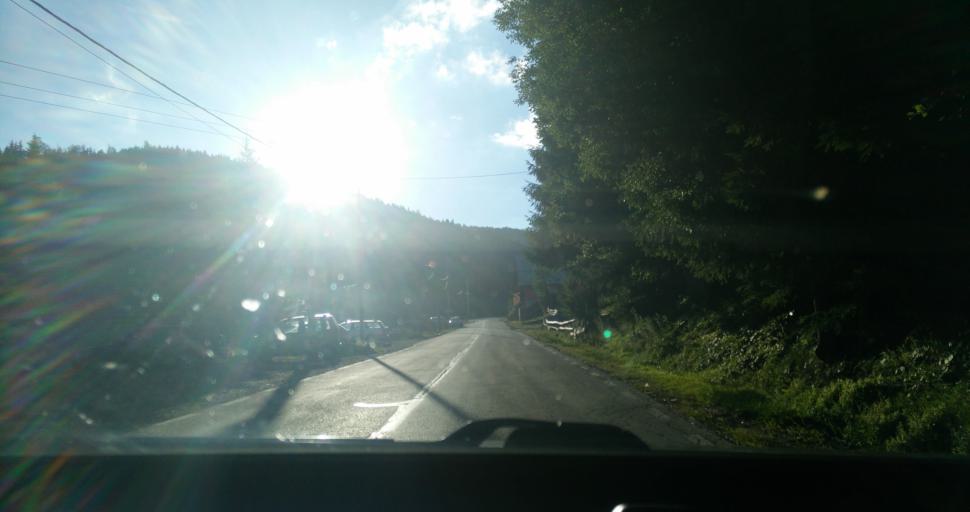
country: RO
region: Alba
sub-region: Comuna Arieseni
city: Arieseni
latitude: 46.5064
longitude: 22.6999
